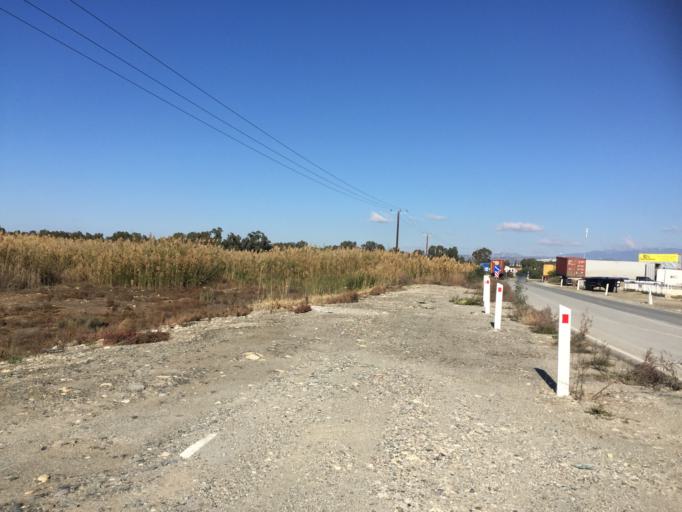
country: CY
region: Limassol
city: Limassol
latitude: 34.6431
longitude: 33.0038
